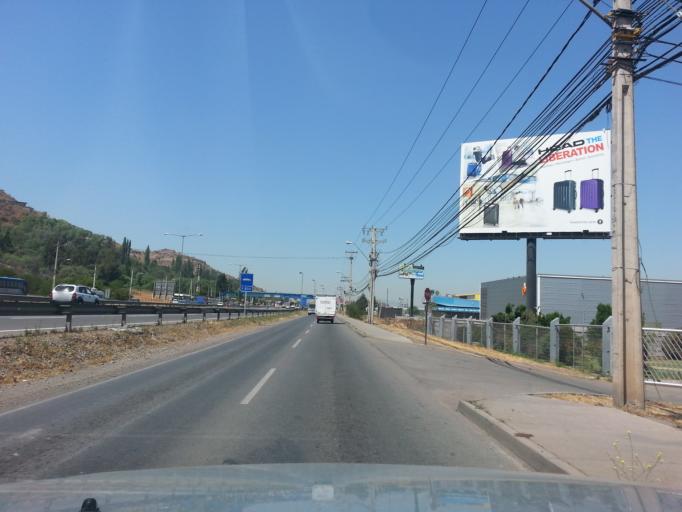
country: CL
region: Santiago Metropolitan
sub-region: Provincia de Chacabuco
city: Chicureo Abajo
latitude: -33.3083
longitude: -70.7011
